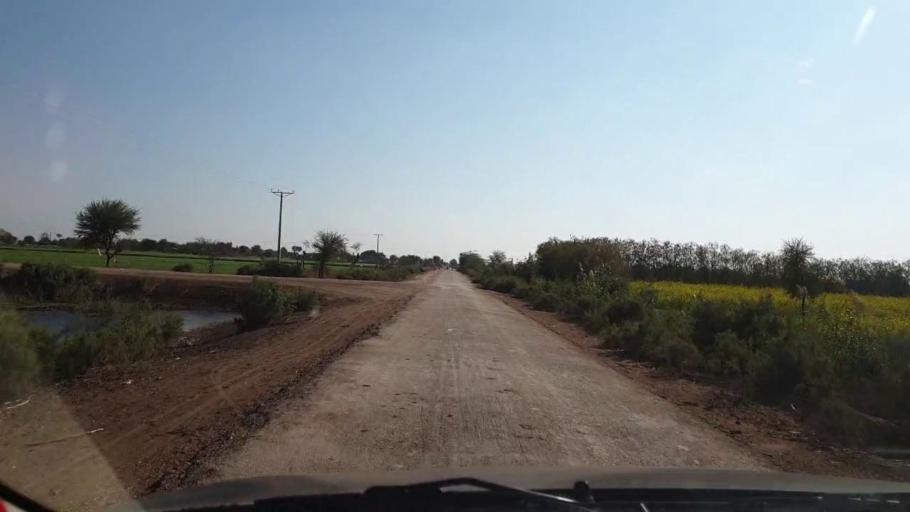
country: PK
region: Sindh
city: Sinjhoro
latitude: 25.9904
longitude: 68.8394
